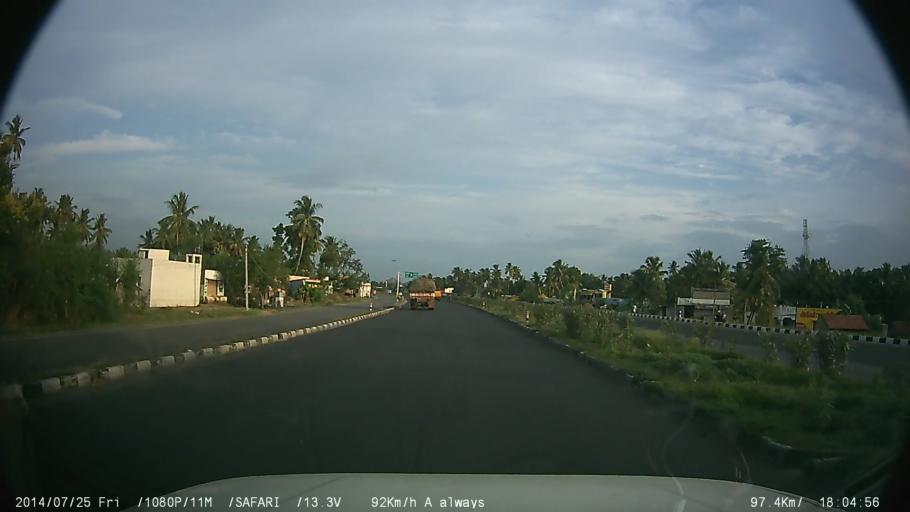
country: IN
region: Tamil Nadu
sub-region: Krishnagiri
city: Kaverippattanam
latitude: 12.4448
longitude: 78.2181
